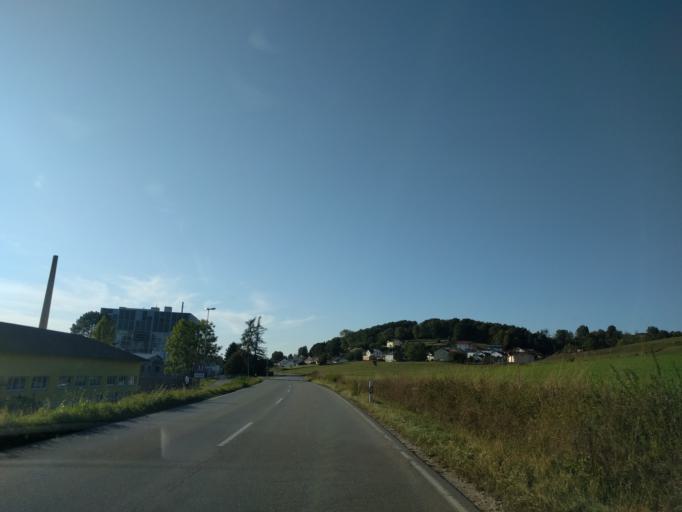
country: DE
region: Bavaria
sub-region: Lower Bavaria
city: Winzer
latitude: 48.7170
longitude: 13.0906
